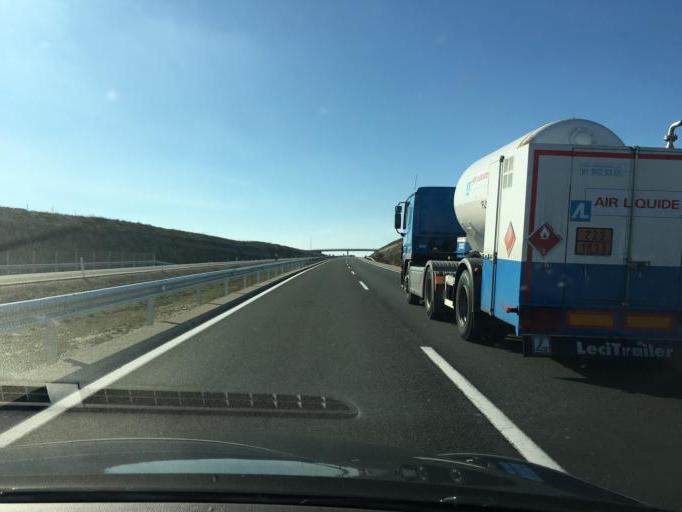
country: ES
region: Castille and Leon
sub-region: Provincia de Burgos
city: Zuneda
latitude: 42.5900
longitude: -3.2343
